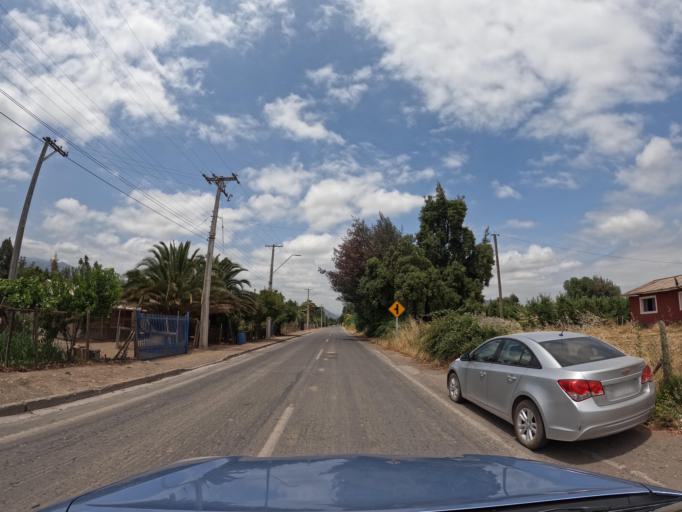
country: CL
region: O'Higgins
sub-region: Provincia de Colchagua
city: Chimbarongo
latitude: -34.7520
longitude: -70.9536
